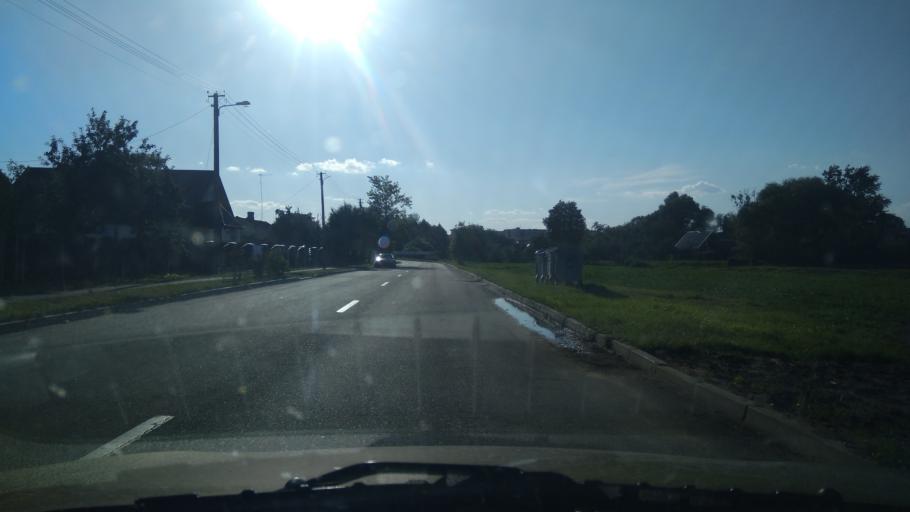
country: BY
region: Brest
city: Byaroza
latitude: 52.5371
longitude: 24.9817
